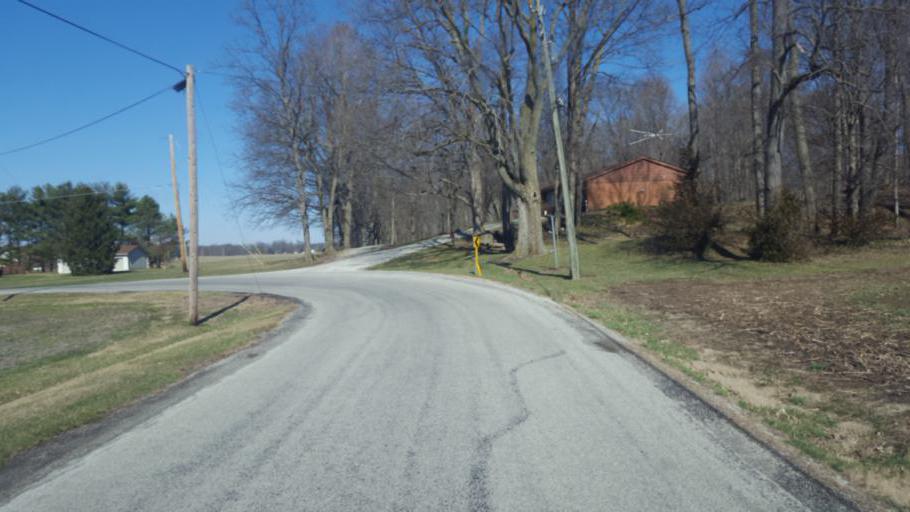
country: US
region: Ohio
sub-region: Marion County
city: Marion
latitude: 40.4981
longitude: -83.0810
